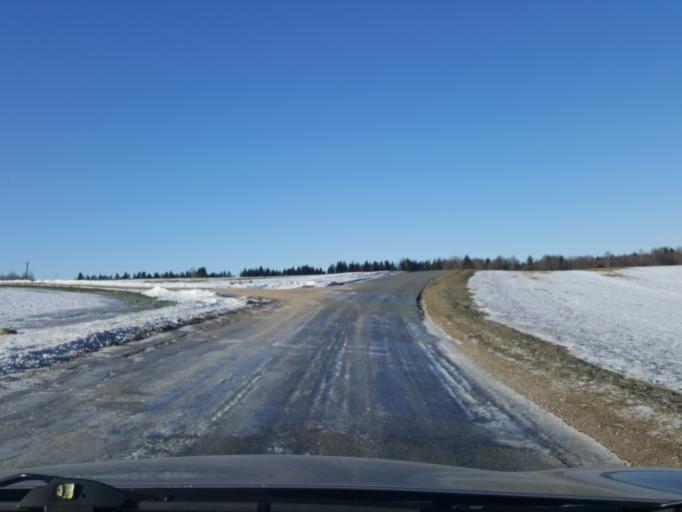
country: EE
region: Viljandimaa
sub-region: Suure-Jaani vald
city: Suure-Jaani
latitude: 58.5327
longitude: 25.5632
